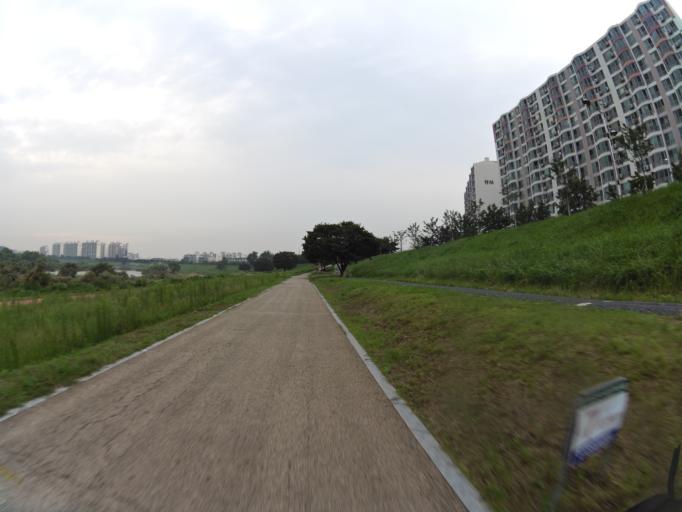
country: KR
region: Gyeongsangbuk-do
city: Gyeongsan-si
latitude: 35.8725
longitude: 128.6787
